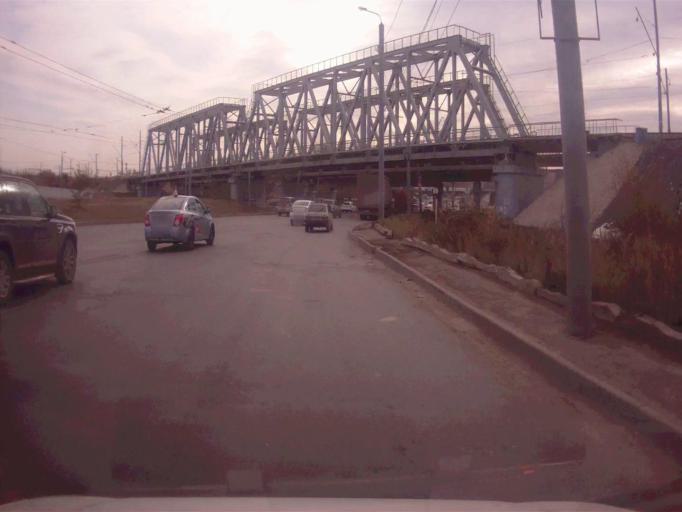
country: RU
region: Chelyabinsk
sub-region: Gorod Chelyabinsk
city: Chelyabinsk
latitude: 55.1550
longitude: 61.4430
